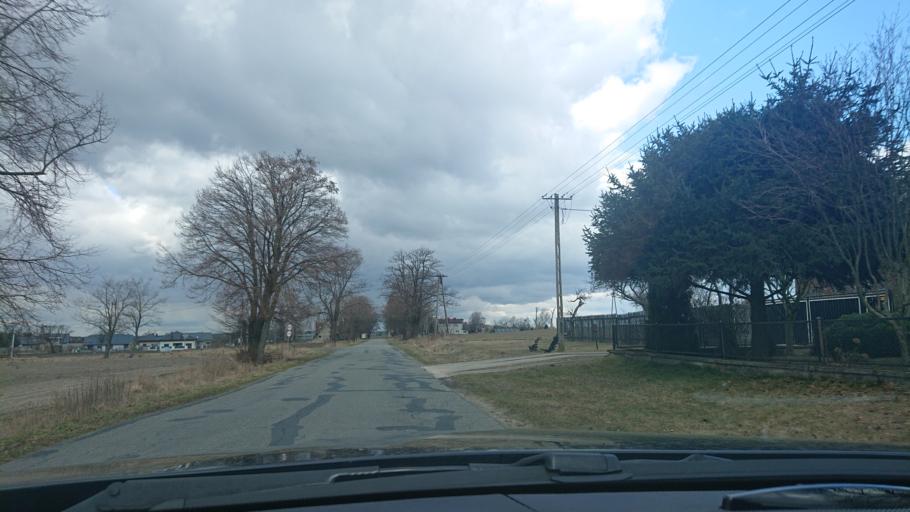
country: PL
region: Greater Poland Voivodeship
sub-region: Powiat gnieznienski
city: Niechanowo
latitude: 52.5718
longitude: 17.7042
